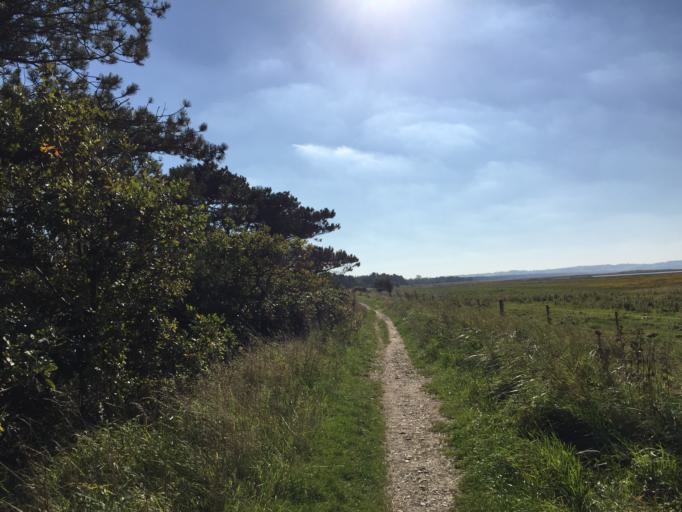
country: DK
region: Zealand
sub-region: Odsherred Kommune
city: Hojby
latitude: 55.8940
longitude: 11.5339
